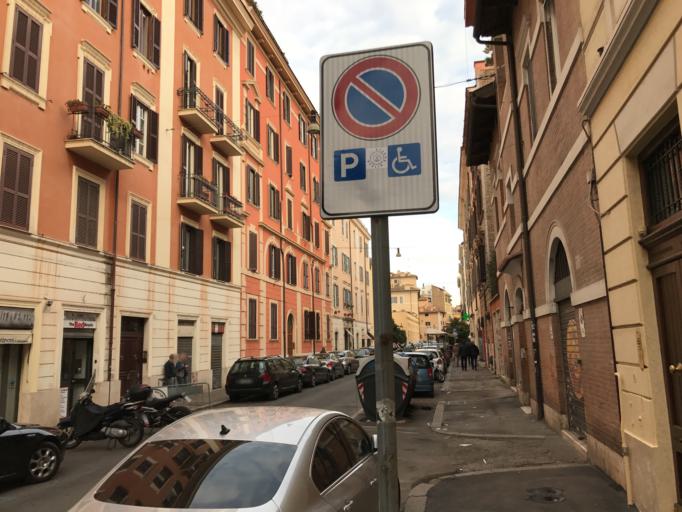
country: IT
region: Latium
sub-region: Citta metropolitana di Roma Capitale
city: Rome
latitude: 41.8893
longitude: 12.4957
